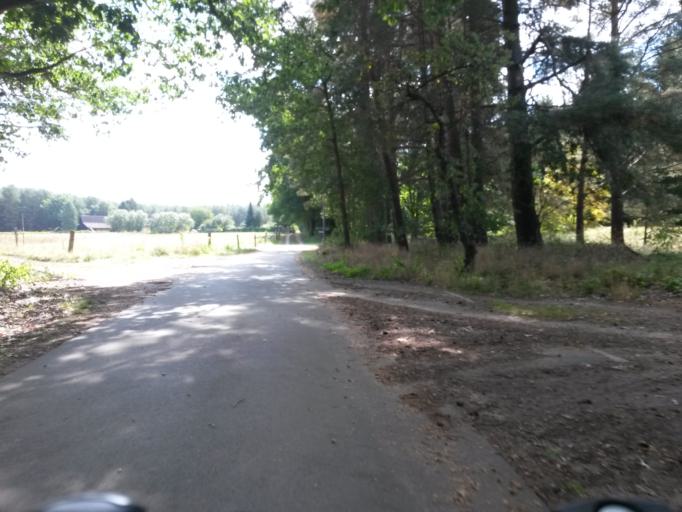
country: DE
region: Brandenburg
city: Templin
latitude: 53.1761
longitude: 13.5150
